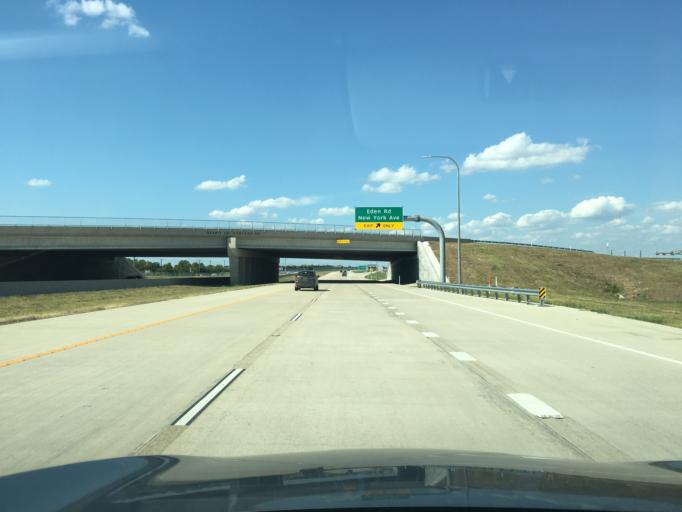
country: US
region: Texas
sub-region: Tarrant County
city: Mansfield
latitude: 32.6086
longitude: -97.0767
